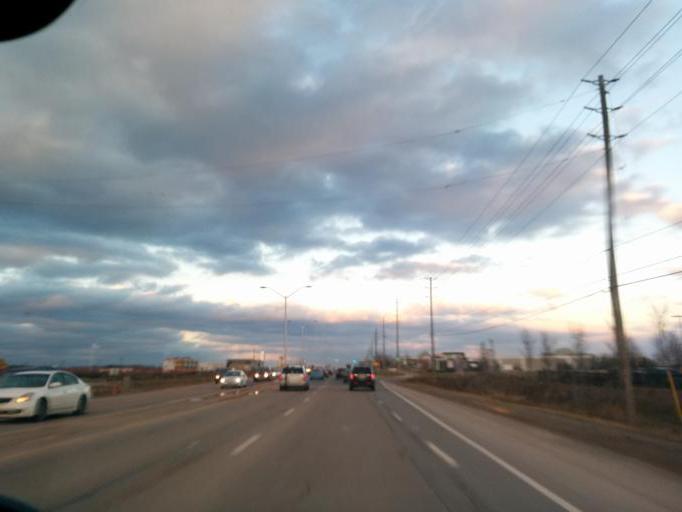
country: CA
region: Ontario
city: Oakville
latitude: 43.4817
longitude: -79.7264
